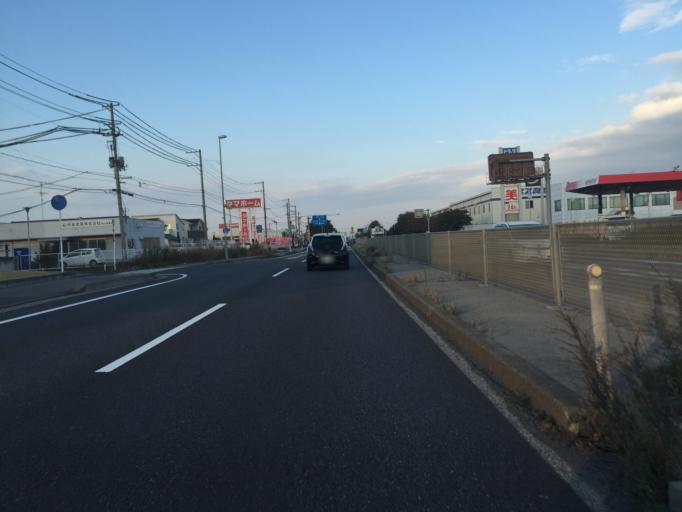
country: JP
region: Fukushima
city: Motomiya
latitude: 37.4898
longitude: 140.3818
